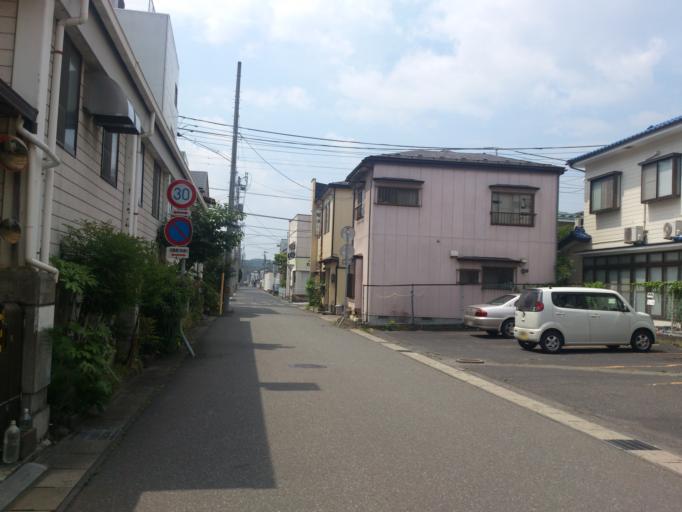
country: JP
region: Iwate
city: Ichinoseki
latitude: 38.9313
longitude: 141.1369
